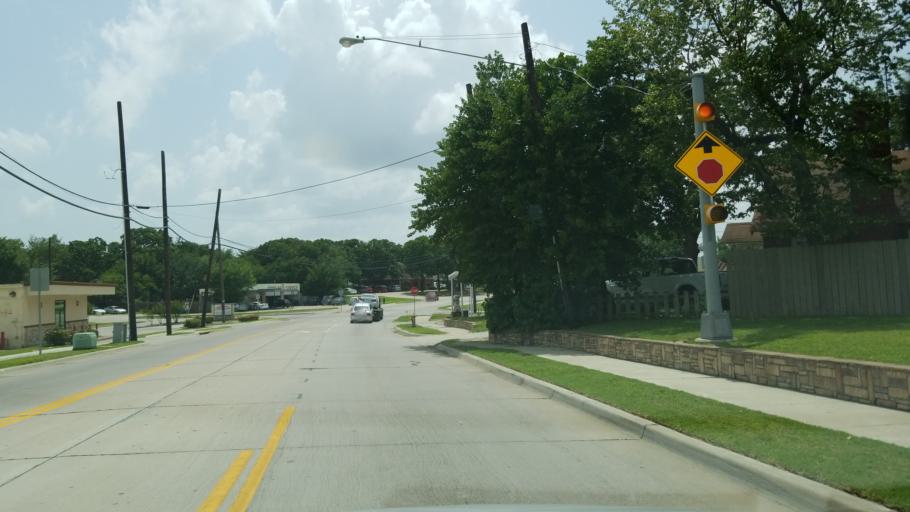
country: US
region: Texas
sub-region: Dallas County
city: Irving
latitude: 32.8304
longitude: -96.9255
